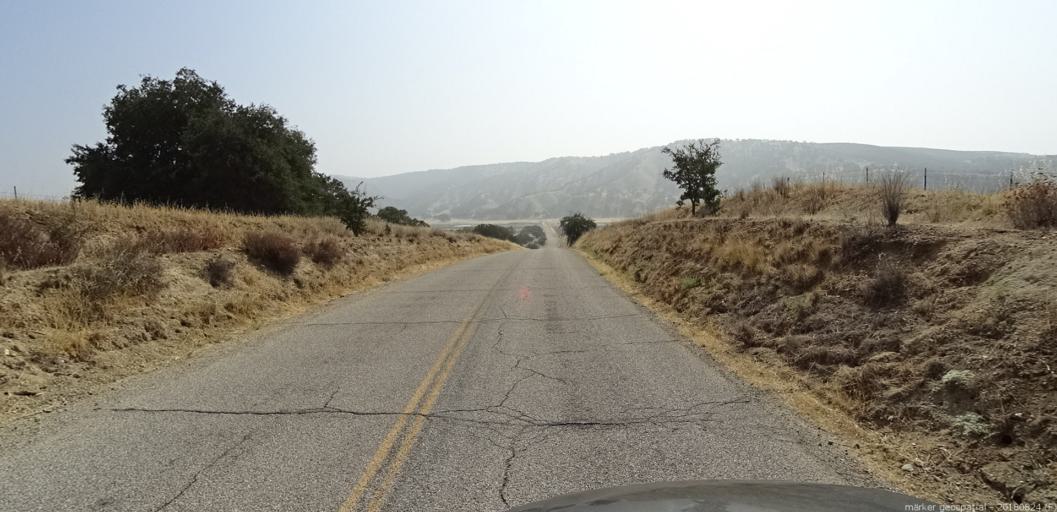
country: US
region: California
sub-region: San Luis Obispo County
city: San Miguel
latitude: 35.9071
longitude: -120.7038
